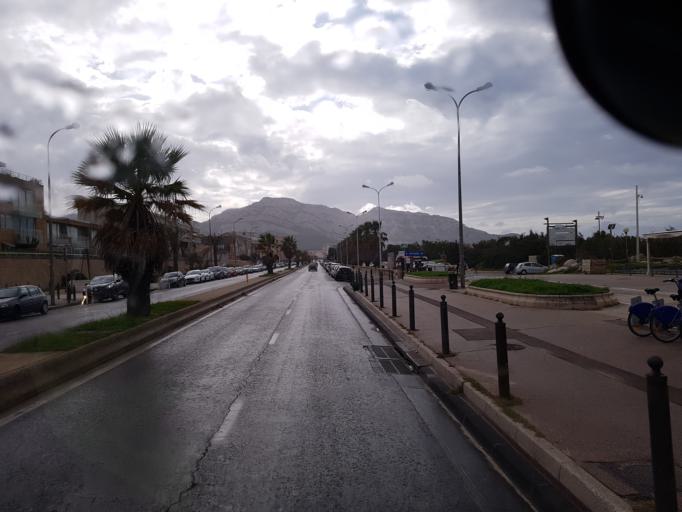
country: FR
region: Provence-Alpes-Cote d'Azur
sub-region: Departement des Bouches-du-Rhone
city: Marseille 08
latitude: 43.2537
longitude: 5.3760
